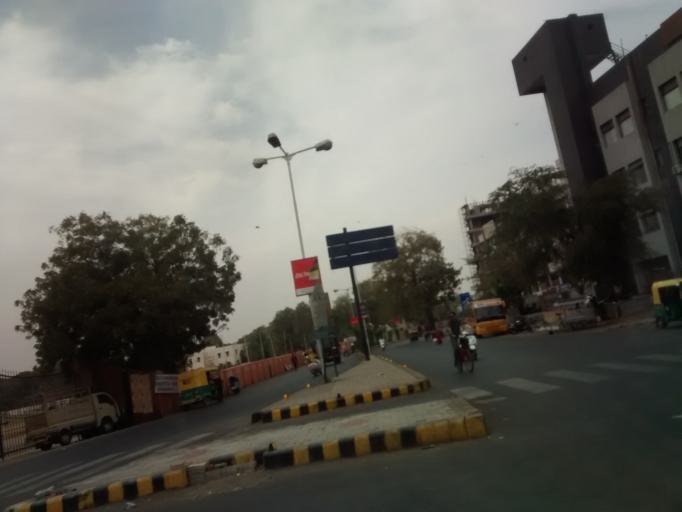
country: IN
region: Gujarat
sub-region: Ahmadabad
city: Ahmedabad
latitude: 23.0736
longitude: 72.5920
